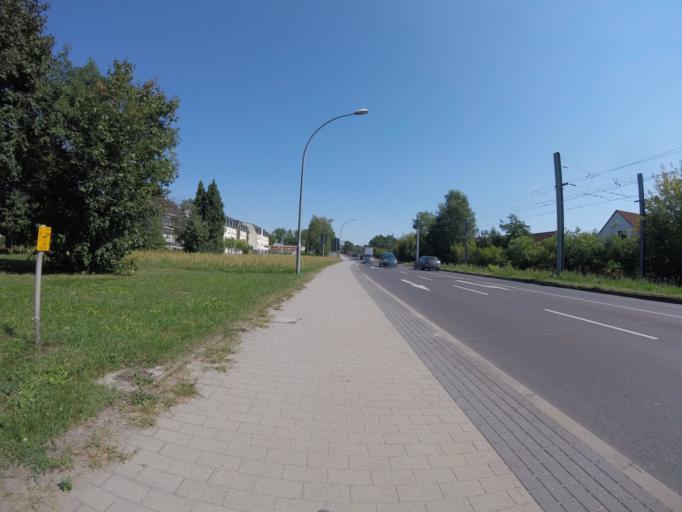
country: DE
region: Brandenburg
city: Mullrose
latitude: 52.2954
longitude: 14.4706
